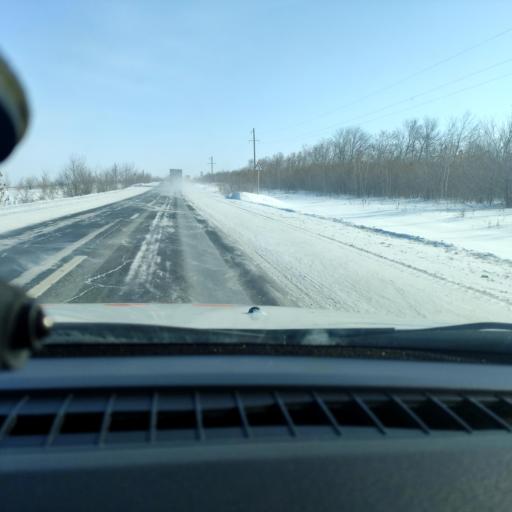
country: RU
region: Samara
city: Smyshlyayevka
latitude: 53.1549
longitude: 50.4509
